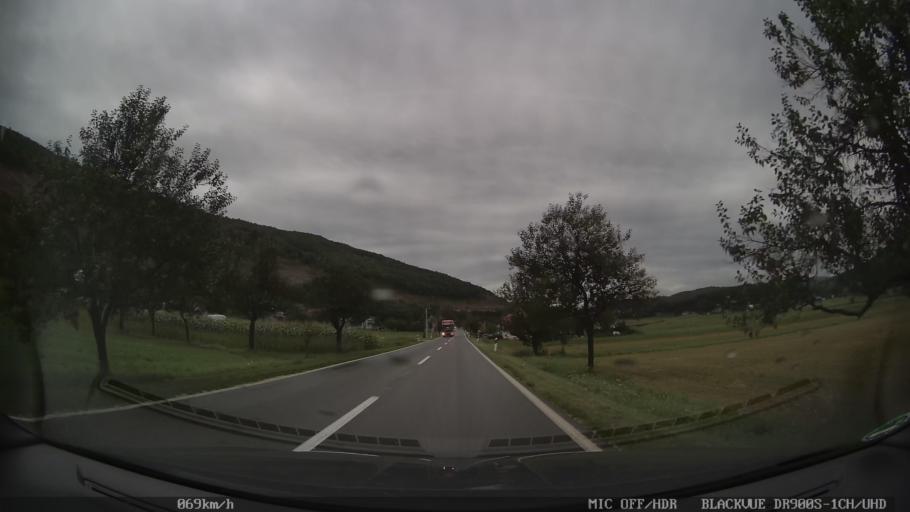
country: HR
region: Licko-Senjska
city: Otocac
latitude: 44.9029
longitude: 15.1762
